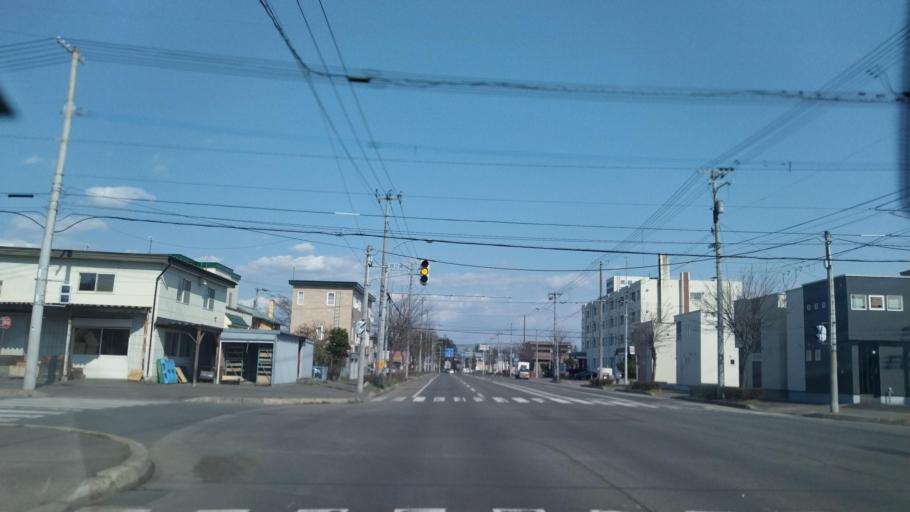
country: JP
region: Hokkaido
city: Obihiro
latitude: 42.8992
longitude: 143.2049
